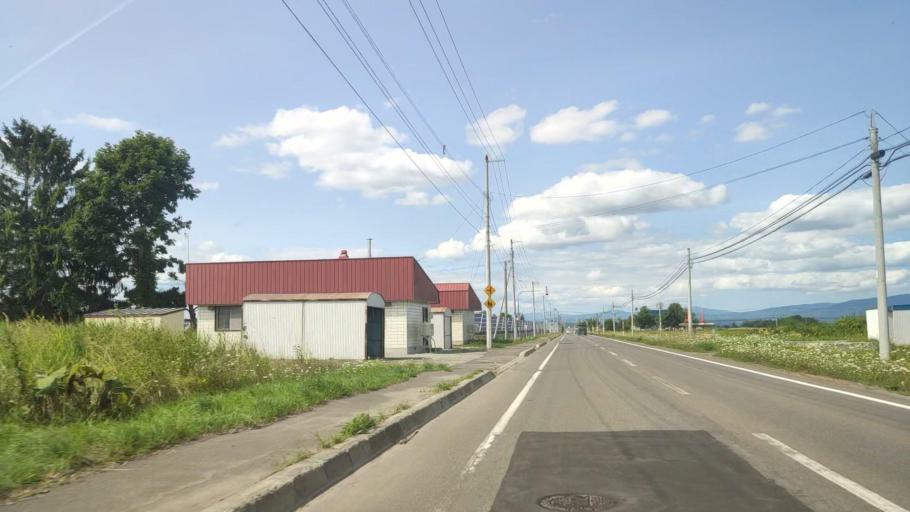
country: JP
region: Hokkaido
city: Nayoro
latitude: 44.2931
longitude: 142.4294
